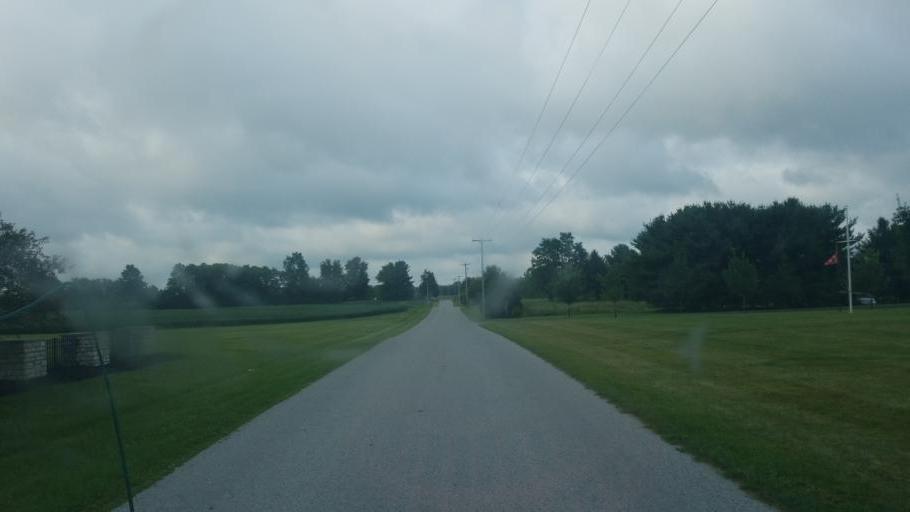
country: US
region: Ohio
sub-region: Morrow County
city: Cardington
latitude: 40.5226
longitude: -82.8594
